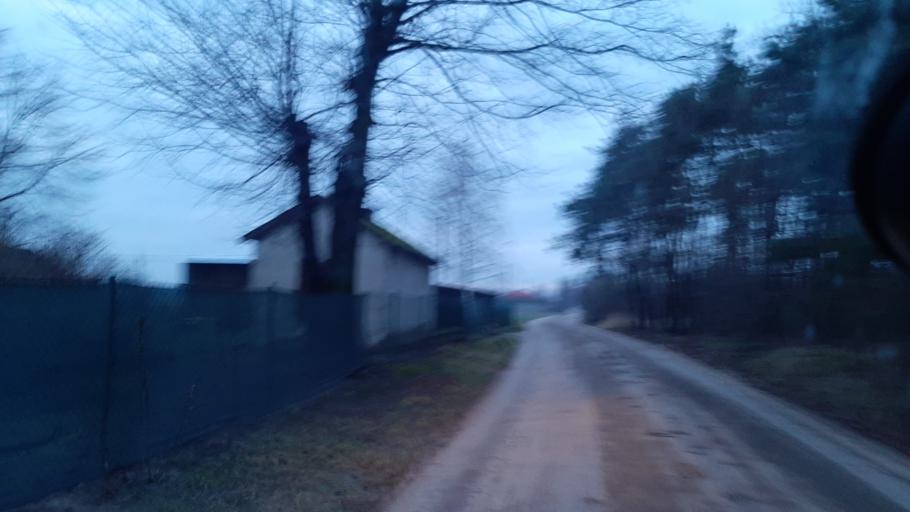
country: PL
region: Lublin Voivodeship
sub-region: Powiat lubartowski
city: Firlej
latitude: 51.5901
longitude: 22.5340
